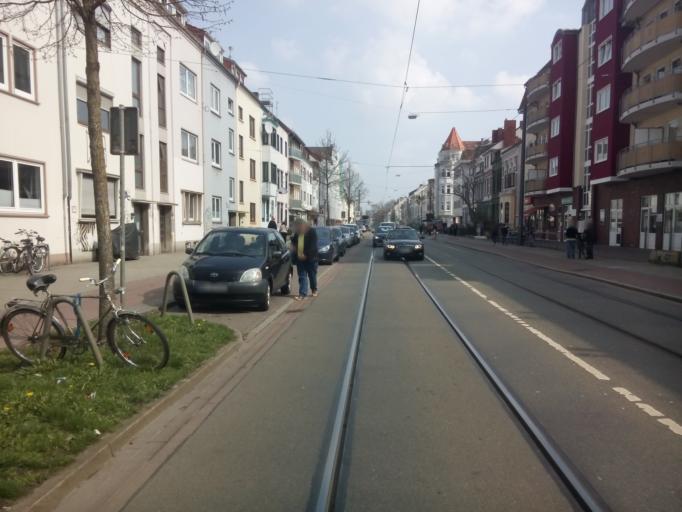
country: DE
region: Bremen
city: Bremen
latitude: 53.0694
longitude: 8.7854
